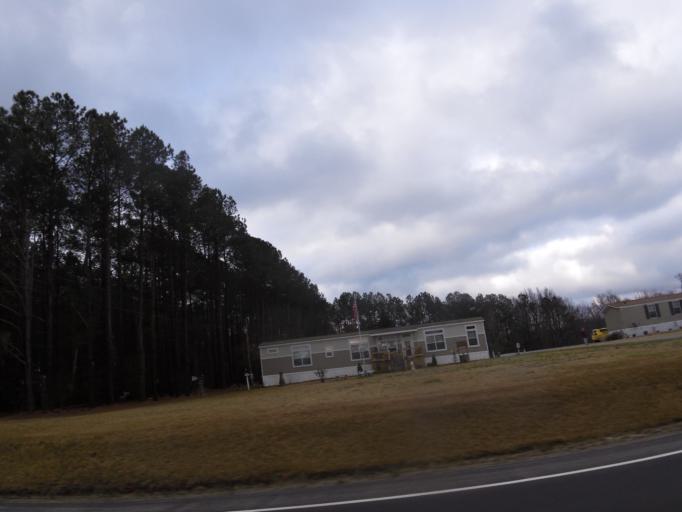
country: US
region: North Carolina
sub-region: Nash County
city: Rocky Mount
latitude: 35.8682
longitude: -77.7328
